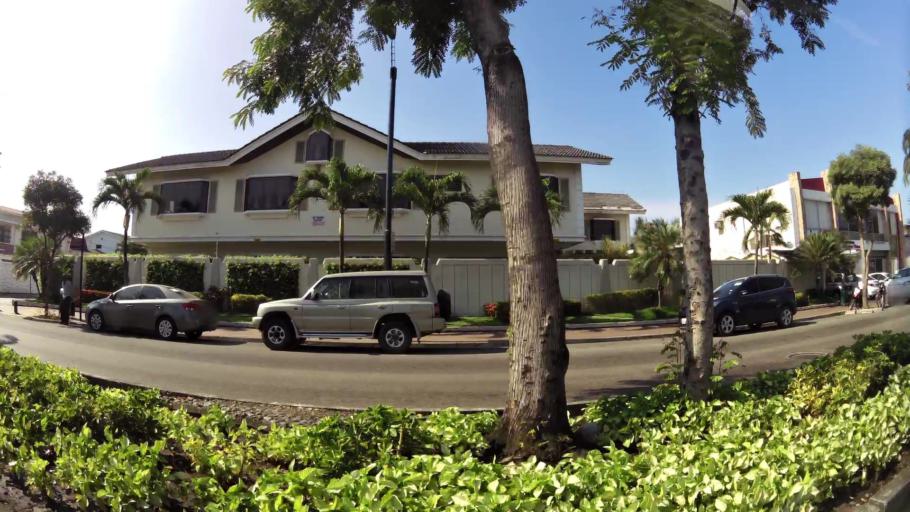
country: EC
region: Guayas
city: Guayaquil
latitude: -2.1705
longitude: -79.9107
